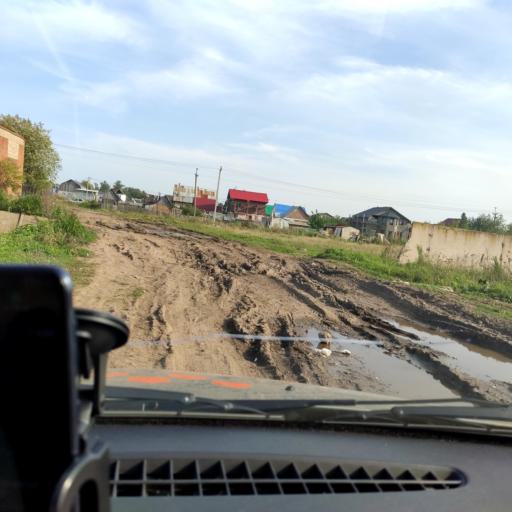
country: RU
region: Bashkortostan
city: Ufa
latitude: 54.8216
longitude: 56.1622
